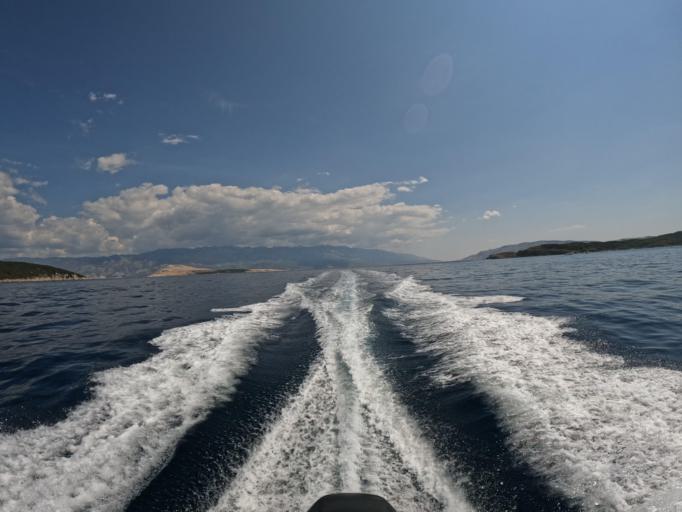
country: HR
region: Primorsko-Goranska
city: Lopar
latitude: 44.8527
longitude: 14.7551
